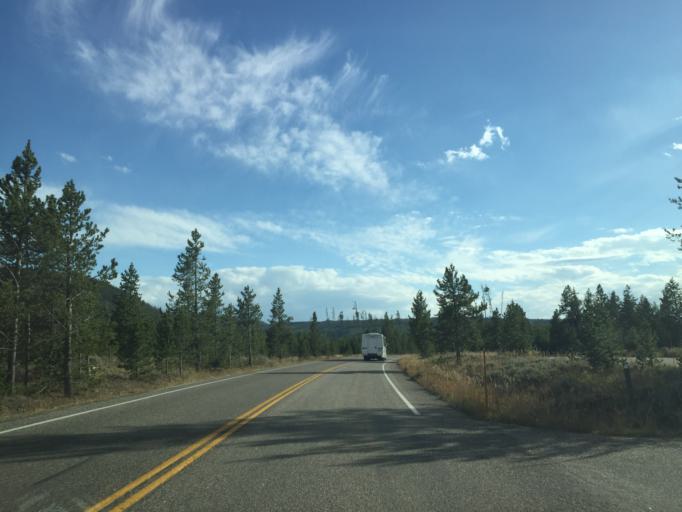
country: US
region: Montana
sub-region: Gallatin County
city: West Yellowstone
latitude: 44.6578
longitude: -110.9904
